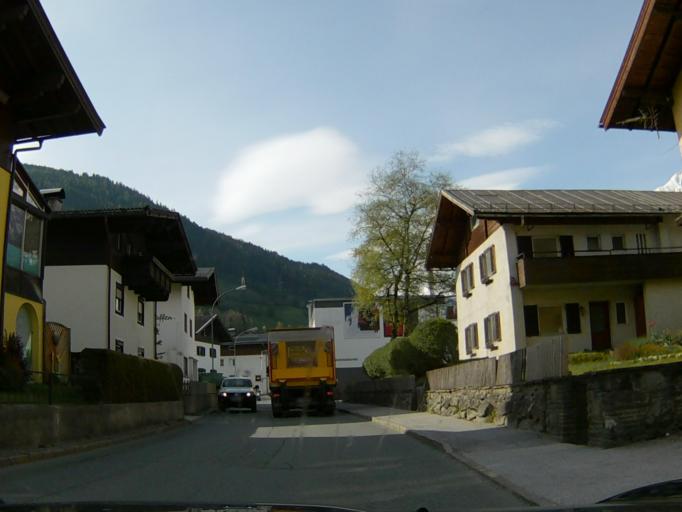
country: AT
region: Salzburg
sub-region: Politischer Bezirk Zell am See
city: Mittersill
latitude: 47.2778
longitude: 12.4842
